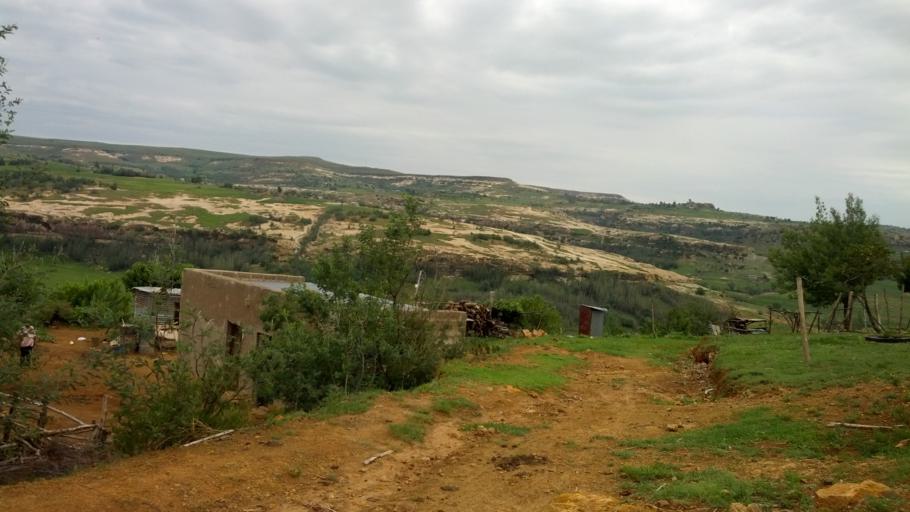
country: LS
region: Berea
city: Teyateyaneng
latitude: -29.1202
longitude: 27.9599
